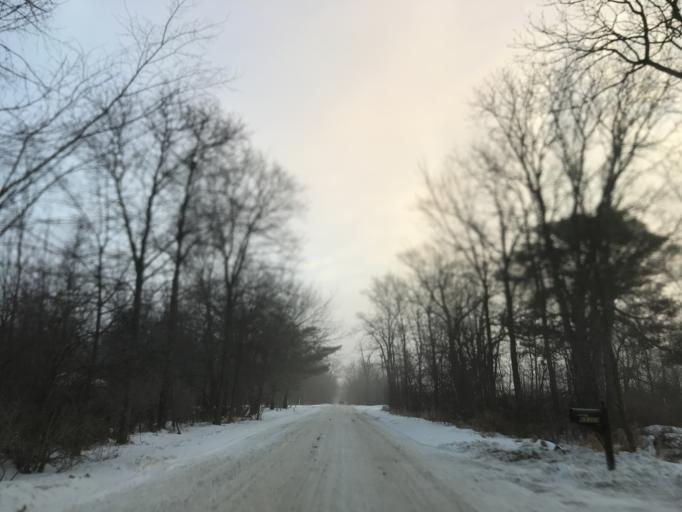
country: US
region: Michigan
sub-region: Oakland County
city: South Lyon
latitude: 42.4916
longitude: -83.5963
